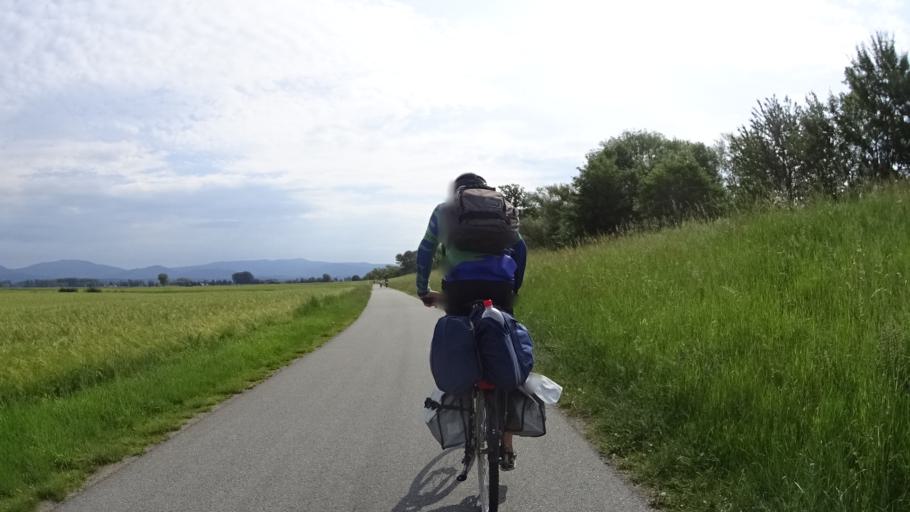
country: DE
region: Bavaria
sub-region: Lower Bavaria
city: Mariaposching
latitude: 48.8267
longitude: 12.8200
